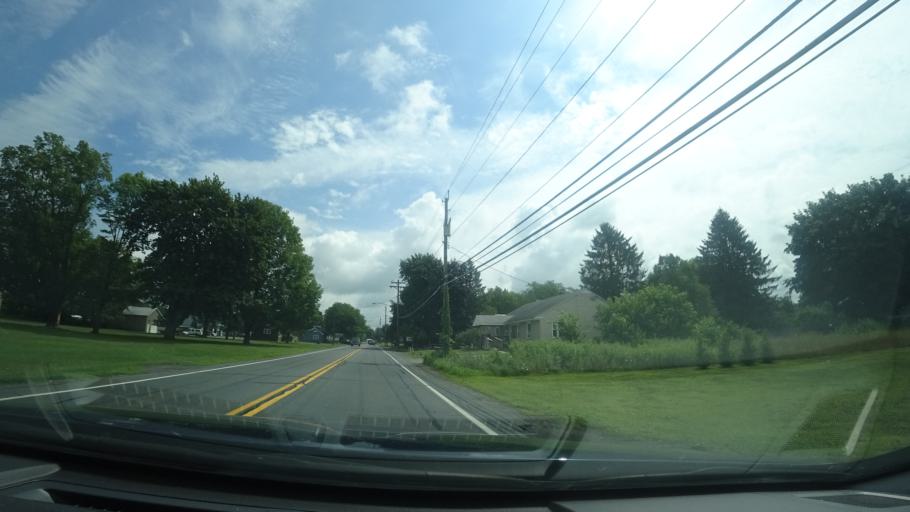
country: US
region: New York
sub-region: Washington County
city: Hudson Falls
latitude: 43.3162
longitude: -73.6019
